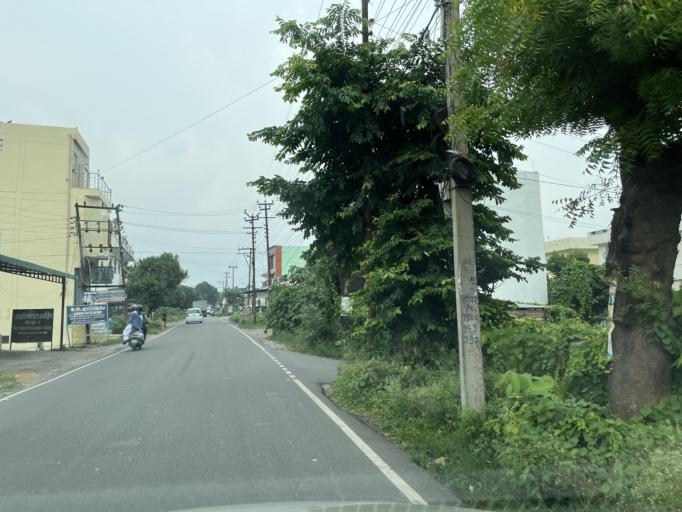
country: IN
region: Uttarakhand
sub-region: Naini Tal
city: Haldwani
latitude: 29.2053
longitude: 79.4922
